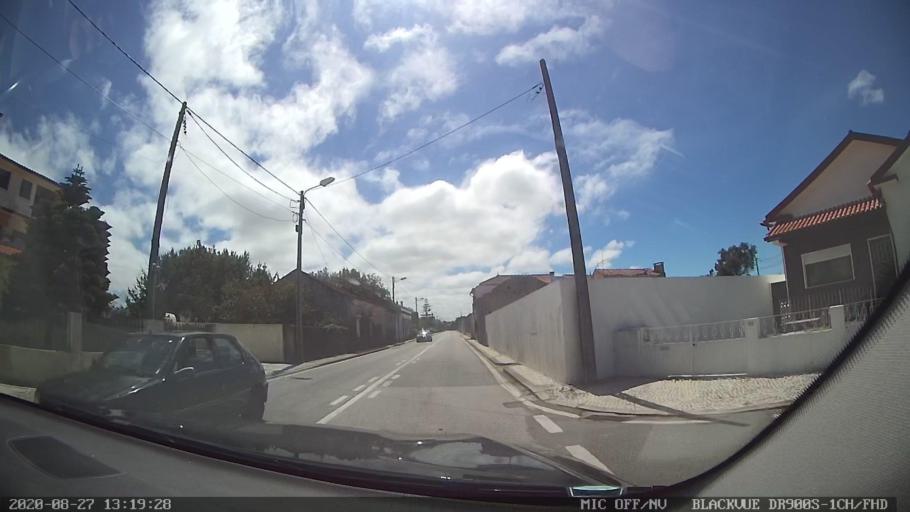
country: PT
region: Aveiro
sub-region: Vagos
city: Vagos
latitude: 40.5636
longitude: -8.6825
